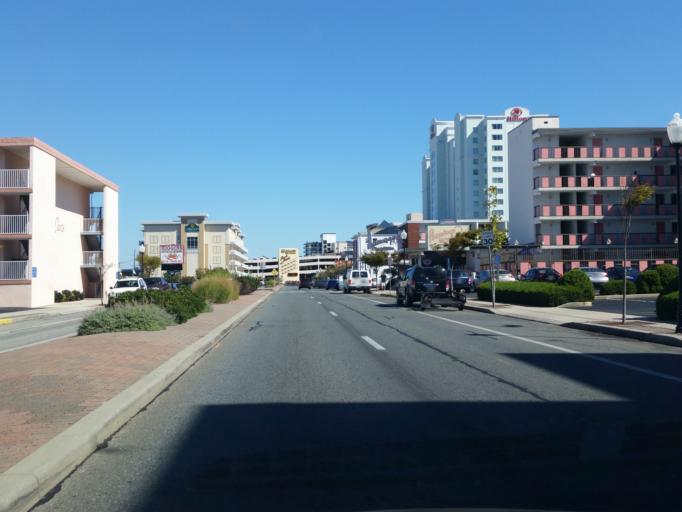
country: US
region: Maryland
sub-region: Worcester County
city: Ocean City
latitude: 38.3588
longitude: -75.0732
